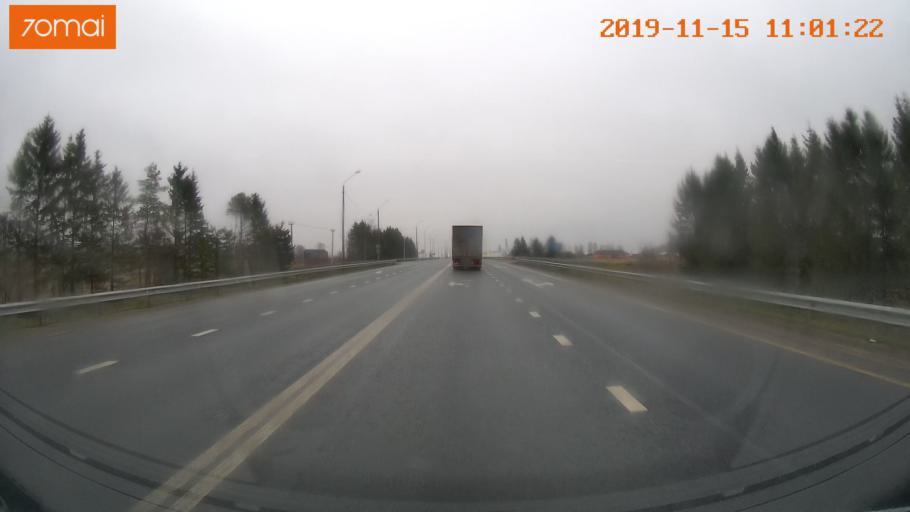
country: RU
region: Vologda
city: Chebsara
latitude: 59.1332
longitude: 38.9190
